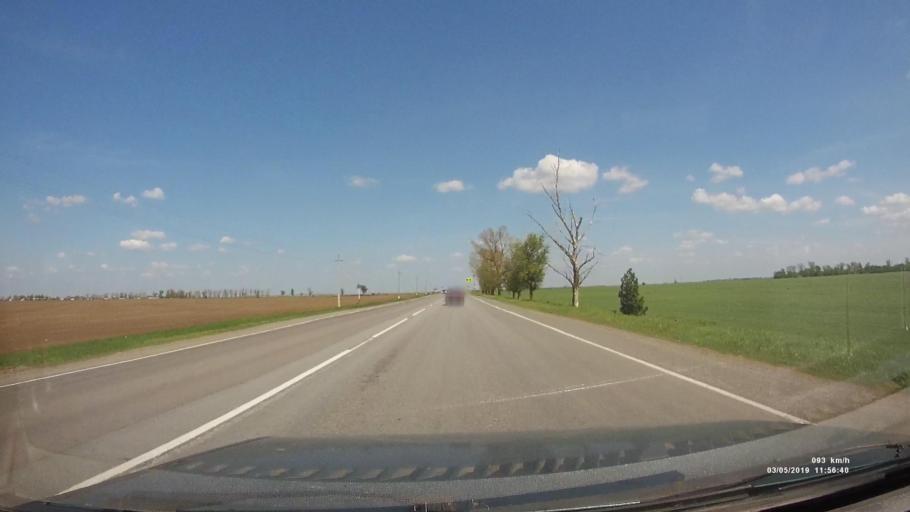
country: RU
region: Rostov
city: Bagayevskaya
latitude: 47.1976
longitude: 40.3032
